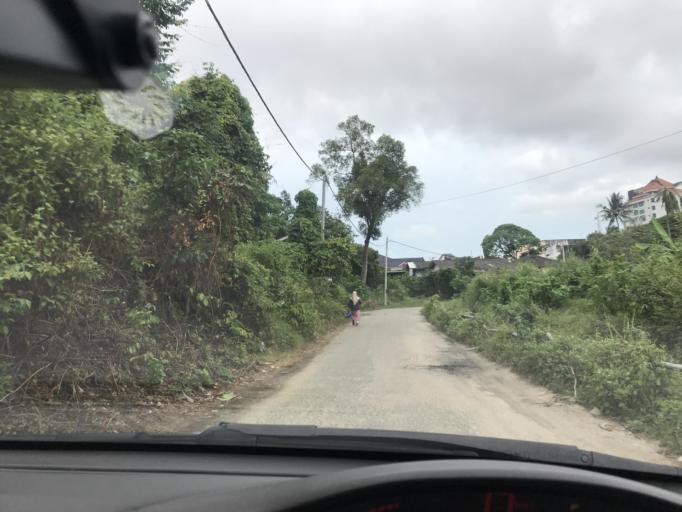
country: MY
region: Kelantan
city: Kota Bharu
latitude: 6.1137
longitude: 102.2358
